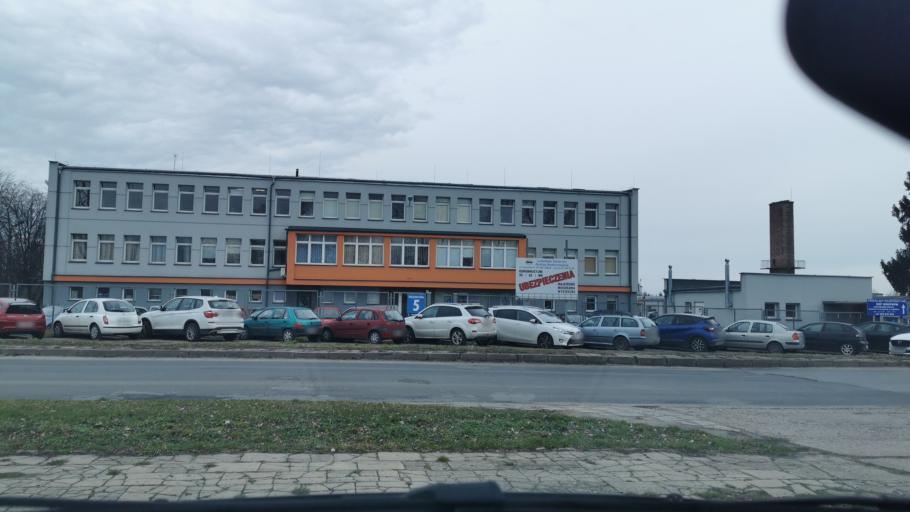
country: PL
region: Lublin Voivodeship
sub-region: Powiat lubelski
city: Lublin
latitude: 51.2168
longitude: 22.5552
